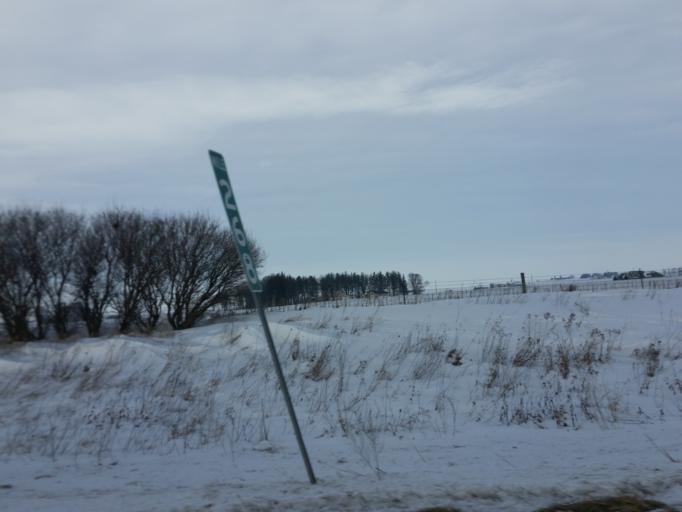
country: US
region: Iowa
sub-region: Delaware County
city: Manchester
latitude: 42.4646
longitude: -91.6215
